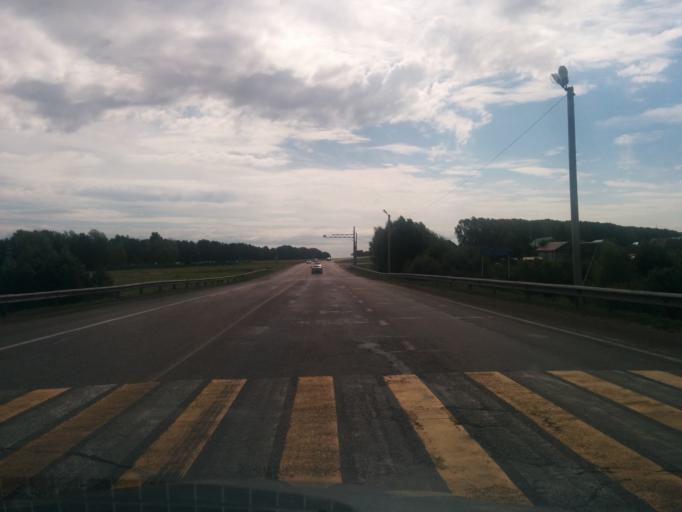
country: RU
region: Bashkortostan
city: Kabakovo
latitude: 54.4660
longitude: 55.9563
